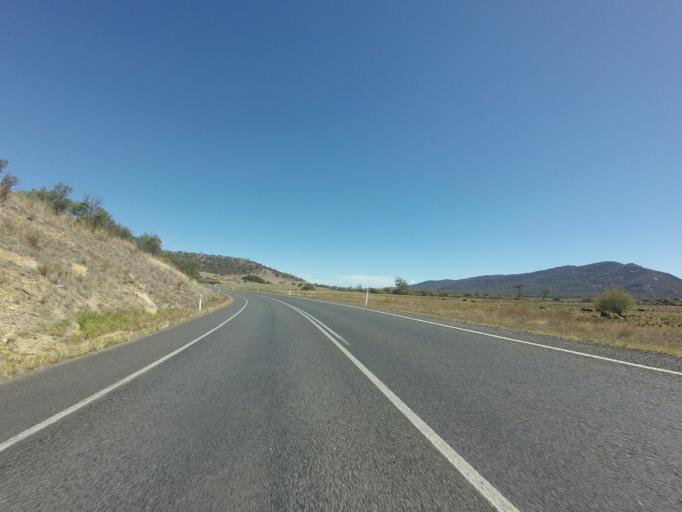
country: AU
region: Tasmania
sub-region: Break O'Day
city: St Helens
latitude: -41.7292
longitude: 147.8218
